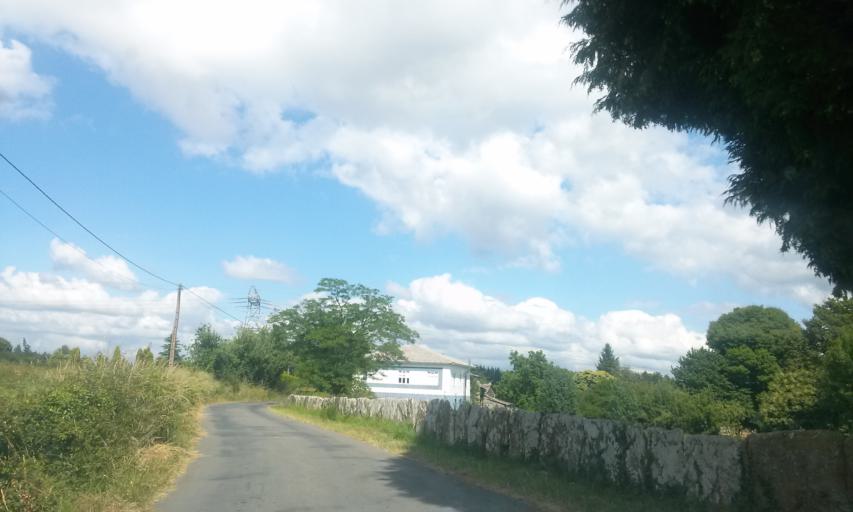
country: ES
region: Galicia
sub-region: Provincia de Lugo
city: Begonte
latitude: 43.1172
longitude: -7.6666
